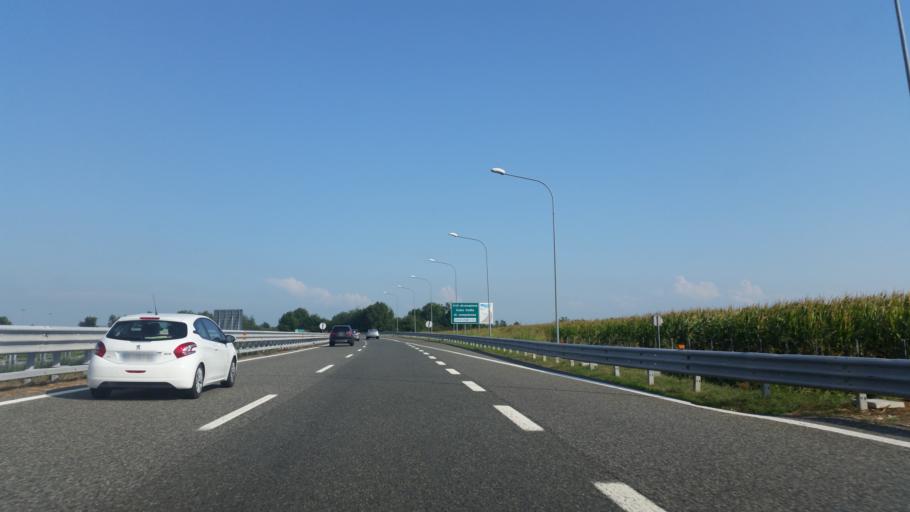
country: IT
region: Piedmont
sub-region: Provincia di Vercelli
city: Santhia
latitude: 45.3706
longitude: 8.1338
